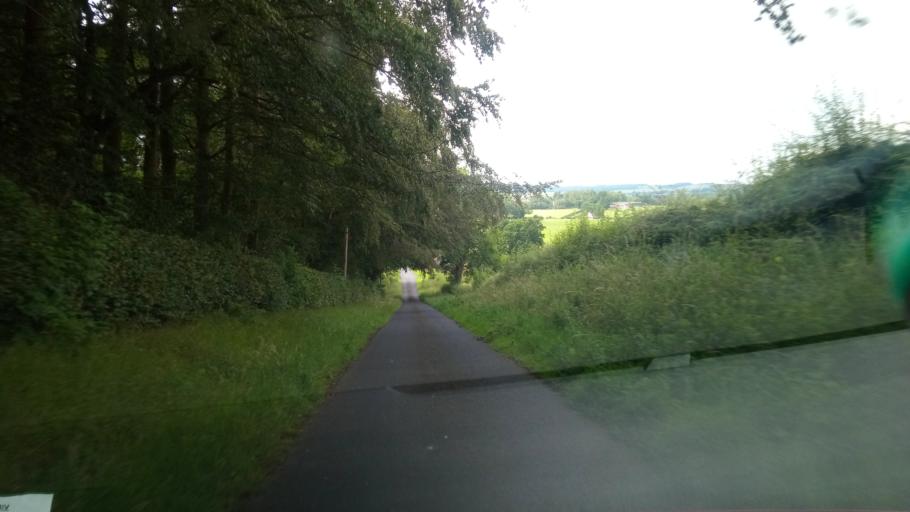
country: GB
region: Scotland
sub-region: The Scottish Borders
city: Hawick
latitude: 55.4393
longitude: -2.6966
